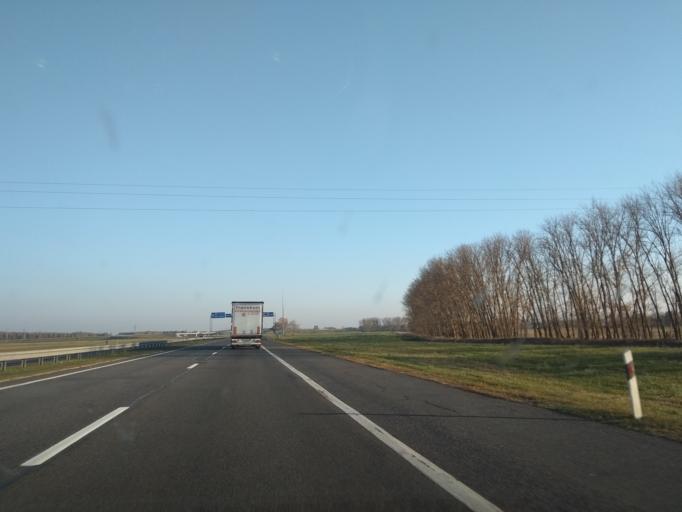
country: BY
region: Brest
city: Kobryn
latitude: 52.1875
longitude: 24.3164
